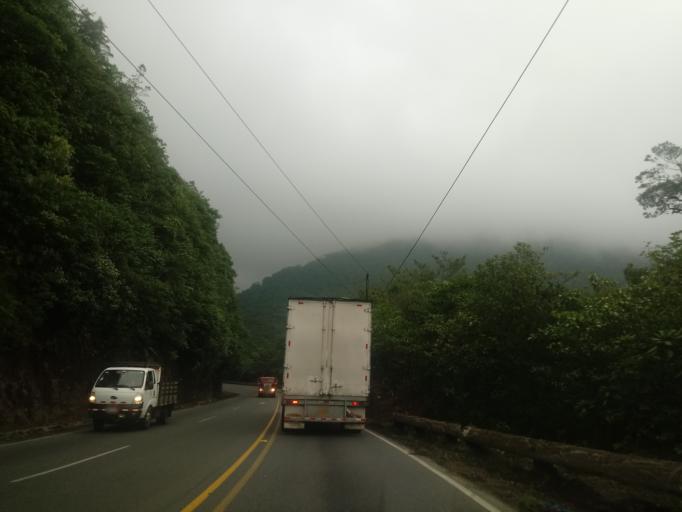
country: CR
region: Heredia
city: Angeles
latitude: 10.0557
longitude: -84.0068
